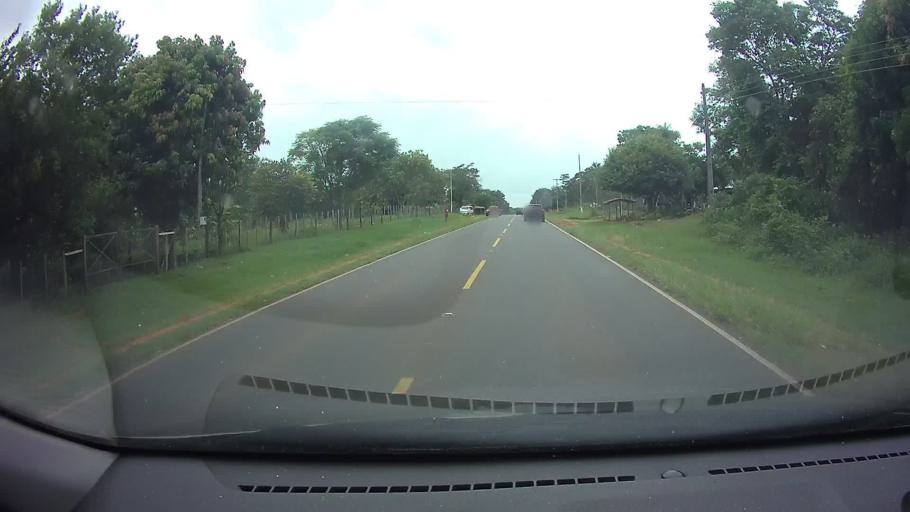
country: PY
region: Paraguari
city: Carapegua
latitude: -25.7513
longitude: -57.2633
